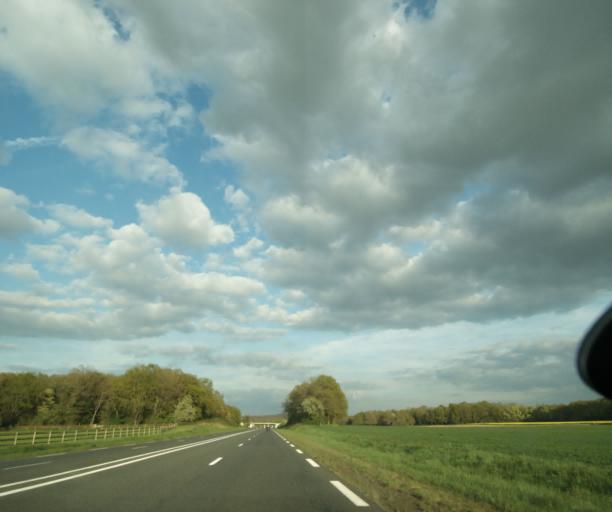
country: FR
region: Ile-de-France
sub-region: Departement de Seine-et-Marne
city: Chailly-en-Biere
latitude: 48.4557
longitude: 2.6073
